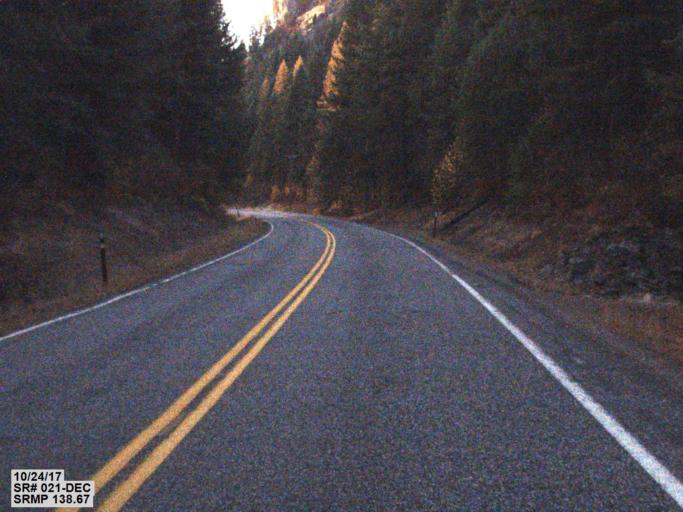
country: US
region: Washington
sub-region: Ferry County
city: Republic
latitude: 48.3702
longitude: -118.7496
